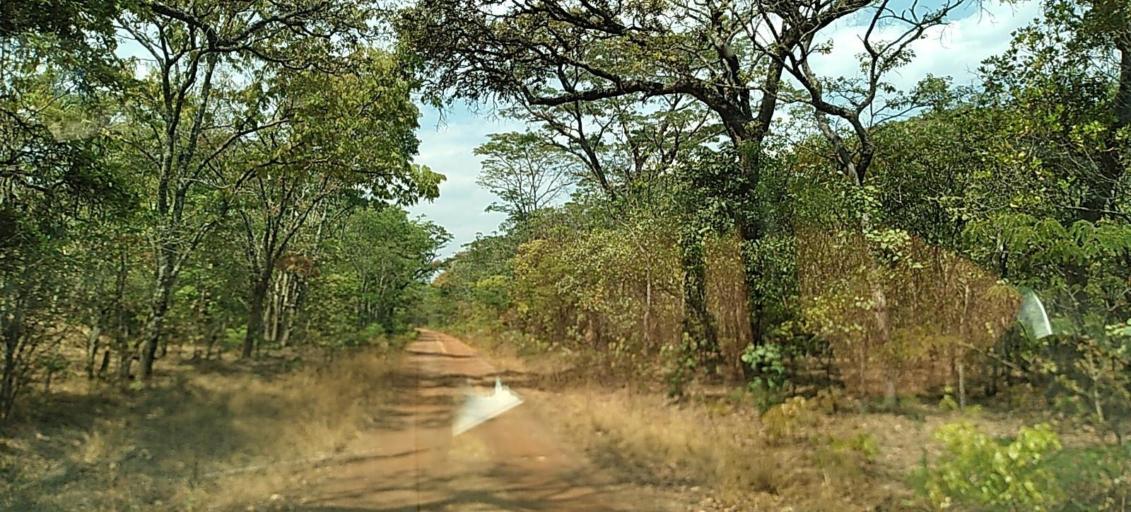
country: ZM
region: Copperbelt
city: Chililabombwe
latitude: -12.4533
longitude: 27.6087
